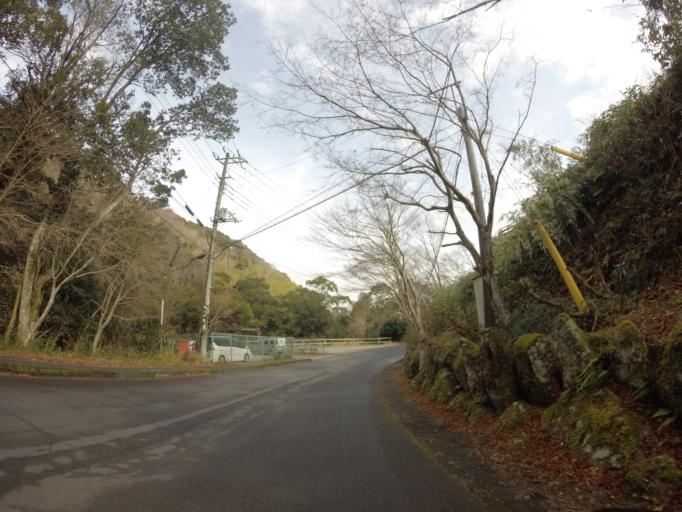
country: JP
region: Shizuoka
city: Heda
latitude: 34.8870
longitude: 138.9241
